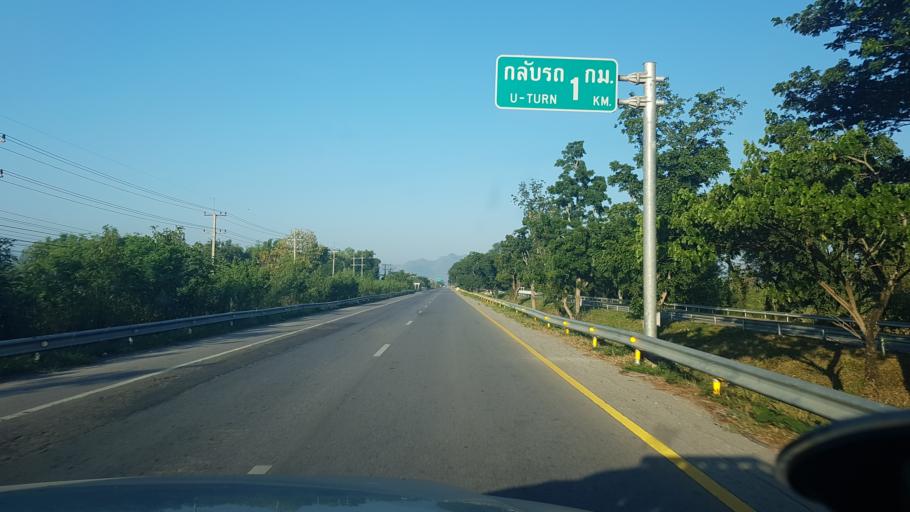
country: TH
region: Chaiyaphum
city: Khon San
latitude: 16.5915
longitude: 101.9722
